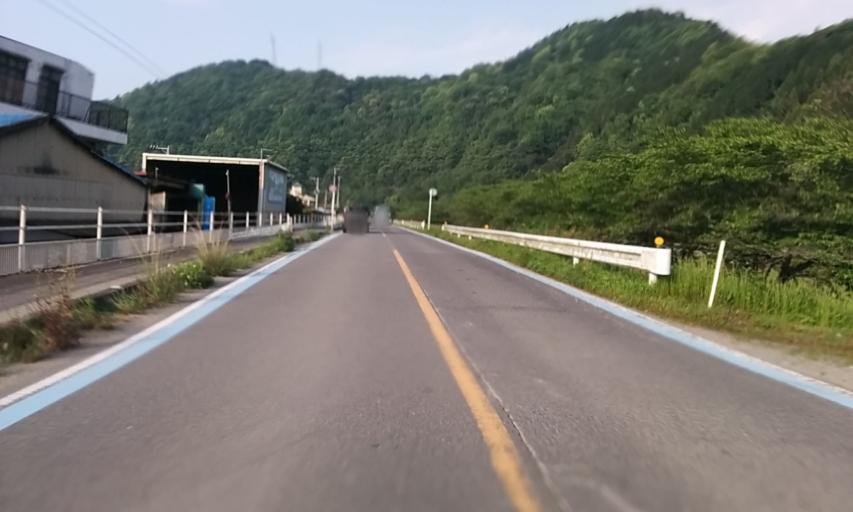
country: JP
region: Ehime
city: Saijo
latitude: 33.8908
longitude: 133.1916
